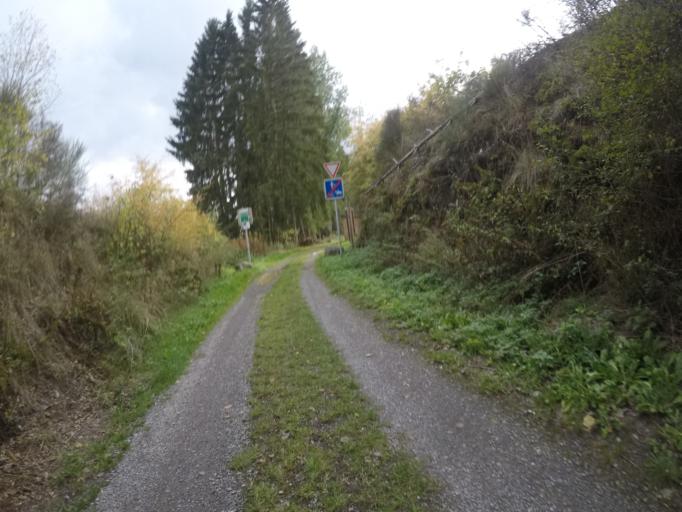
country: BE
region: Wallonia
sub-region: Province du Luxembourg
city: Fauvillers
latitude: 49.8903
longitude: 5.6760
